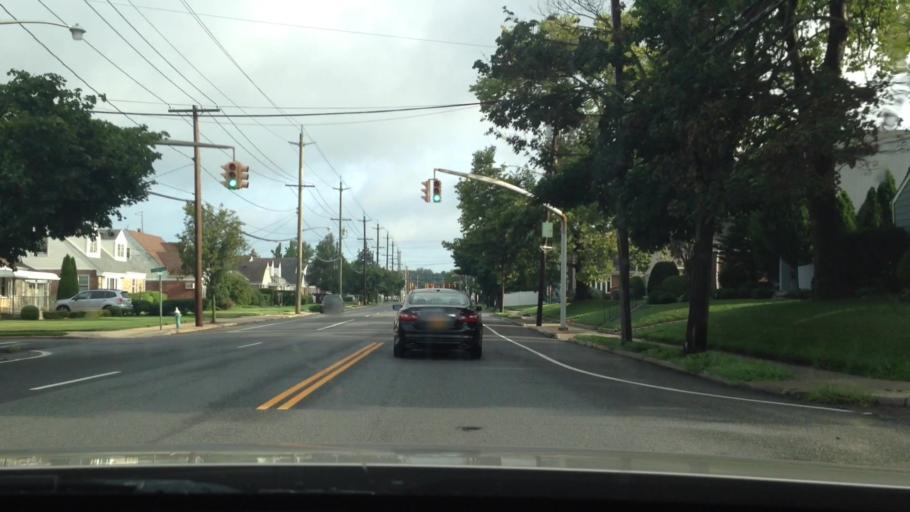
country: US
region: New York
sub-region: Nassau County
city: Manhasset Hills
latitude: 40.7520
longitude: -73.6868
